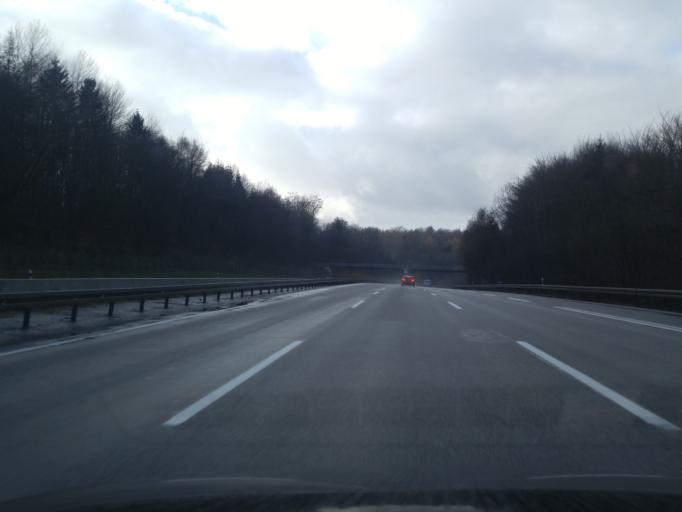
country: DE
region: Hesse
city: Schwarzenborn
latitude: 50.9447
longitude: 9.5283
